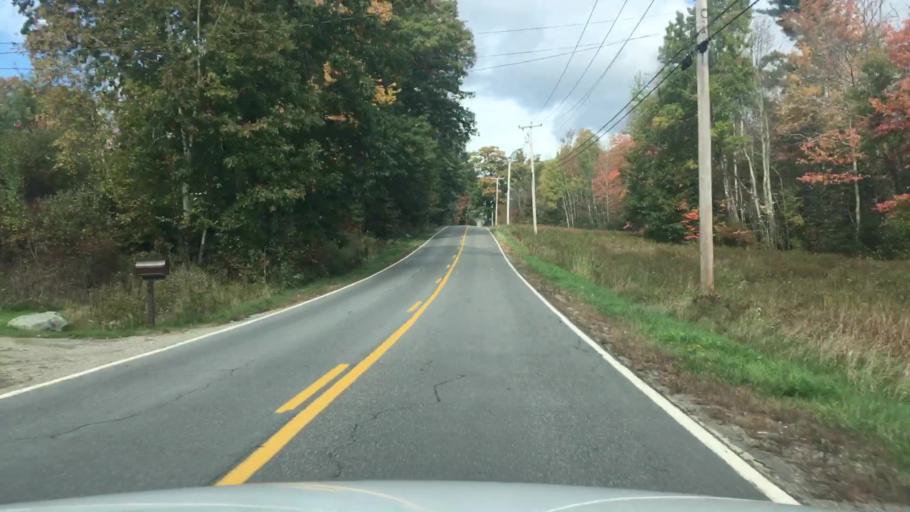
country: US
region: Maine
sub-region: Knox County
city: Hope
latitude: 44.3008
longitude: -69.1105
